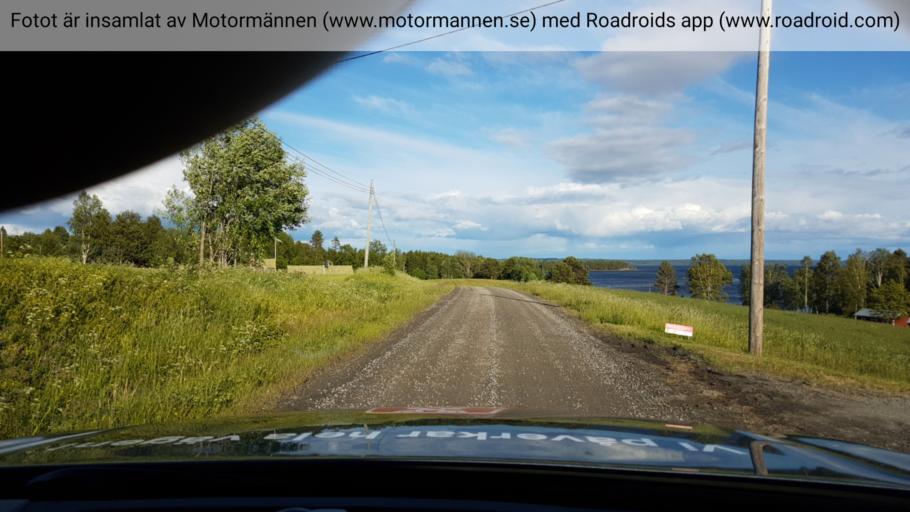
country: SE
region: Jaemtland
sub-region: Bergs Kommun
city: Hoverberg
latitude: 62.9390
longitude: 14.3960
